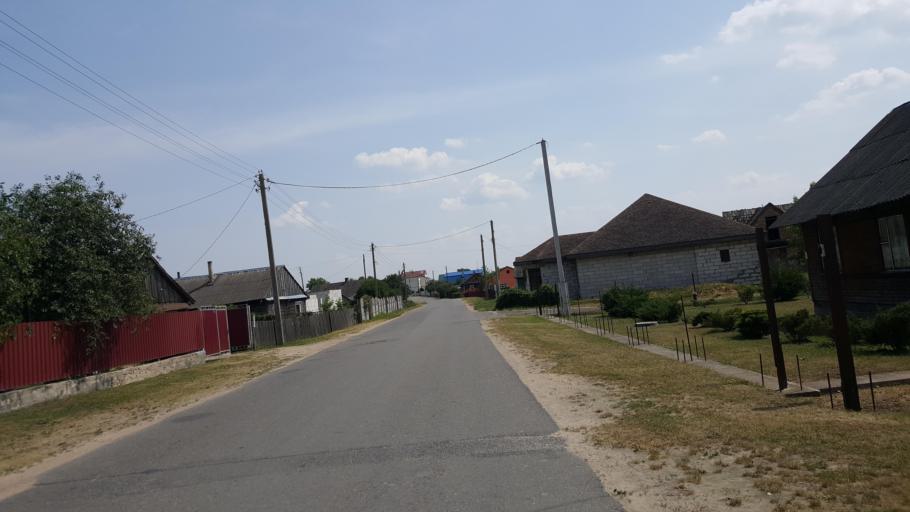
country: BY
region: Brest
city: Kamyanyets
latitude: 52.3283
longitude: 23.7794
